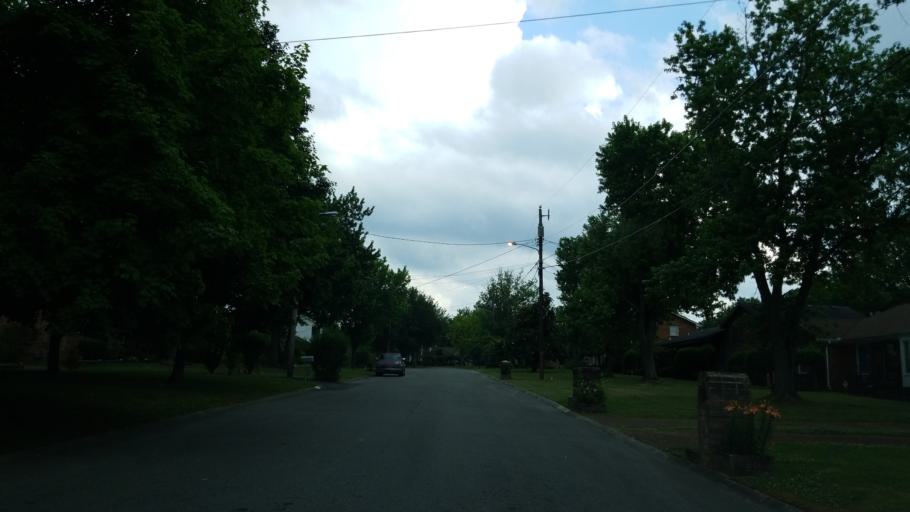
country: US
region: Tennessee
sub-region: Rutherford County
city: La Vergne
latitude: 36.0970
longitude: -86.6109
